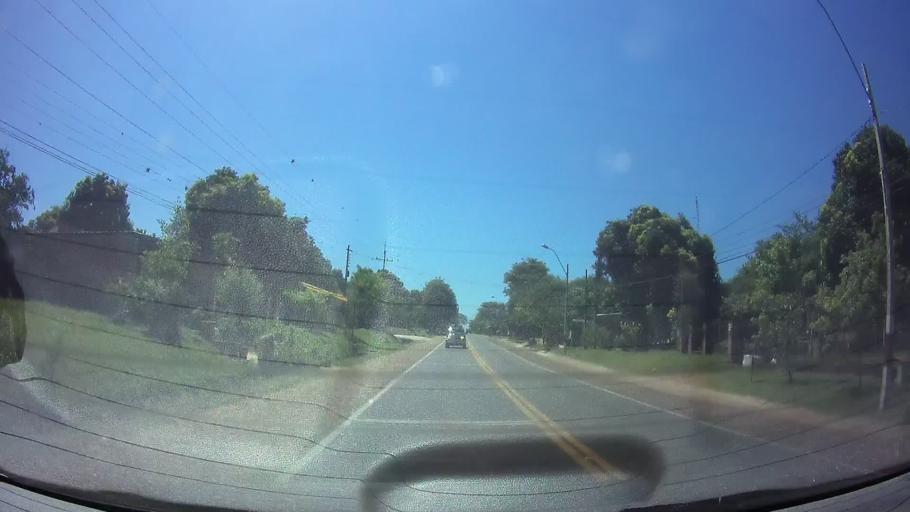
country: PY
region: Central
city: Aregua
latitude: -25.3029
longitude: -57.4030
